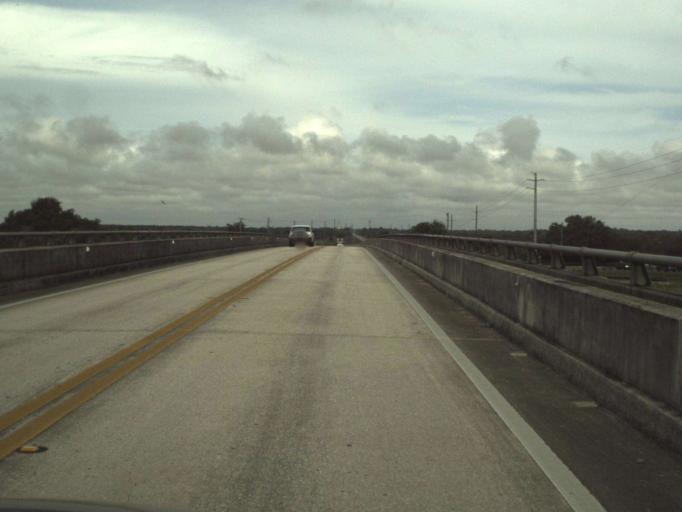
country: US
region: Florida
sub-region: Seminole County
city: Geneva
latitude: 28.7140
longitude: -81.0337
